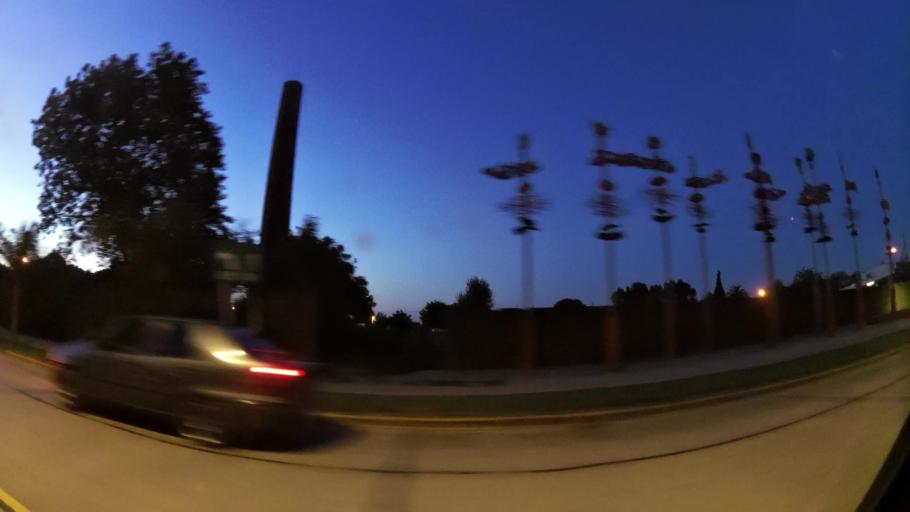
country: AR
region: Buenos Aires
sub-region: Partido de Quilmes
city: Quilmes
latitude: -34.7564
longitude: -58.1990
